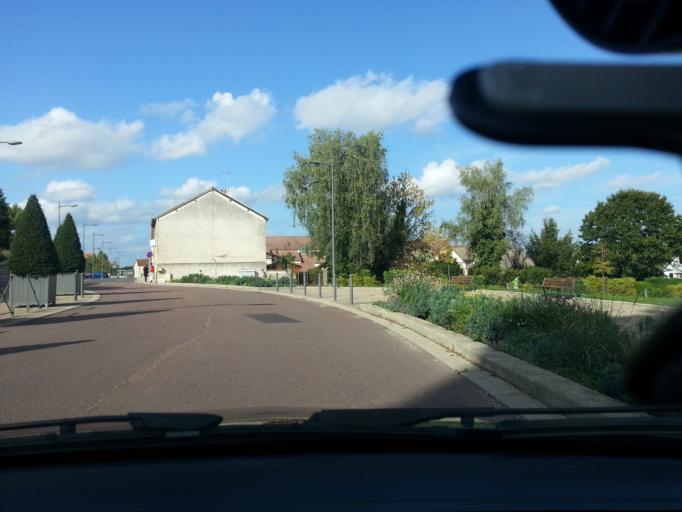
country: FR
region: Bourgogne
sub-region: Departement de Saone-et-Loire
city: Chatenoy-le-Royal
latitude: 46.7937
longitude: 4.8106
